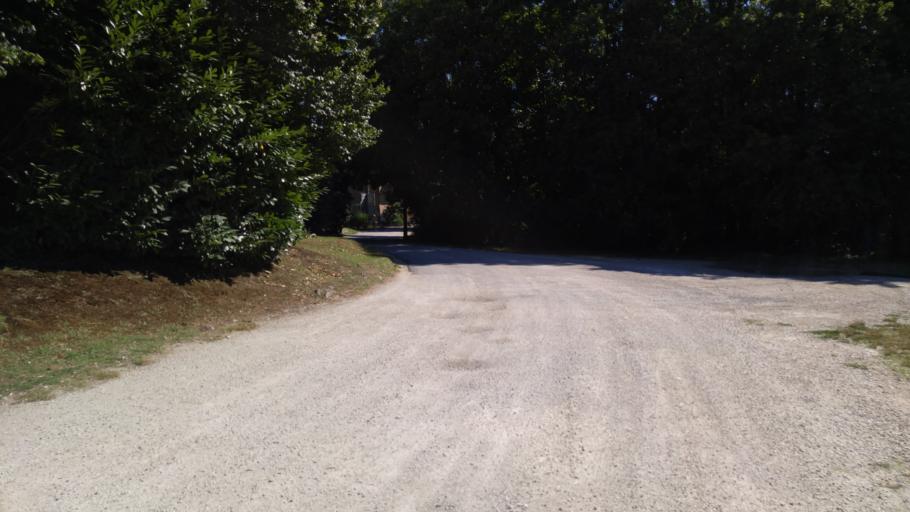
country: IT
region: The Marches
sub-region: Provincia di Pesaro e Urbino
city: Pesaro
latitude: 43.9045
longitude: 12.8968
